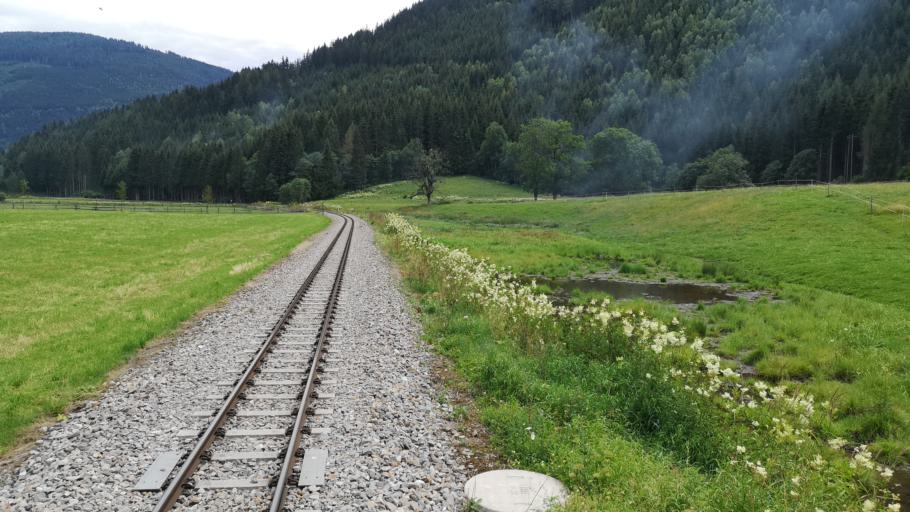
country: AT
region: Styria
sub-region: Politischer Bezirk Murau
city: Stadl an der Mur
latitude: 47.0828
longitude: 13.9644
